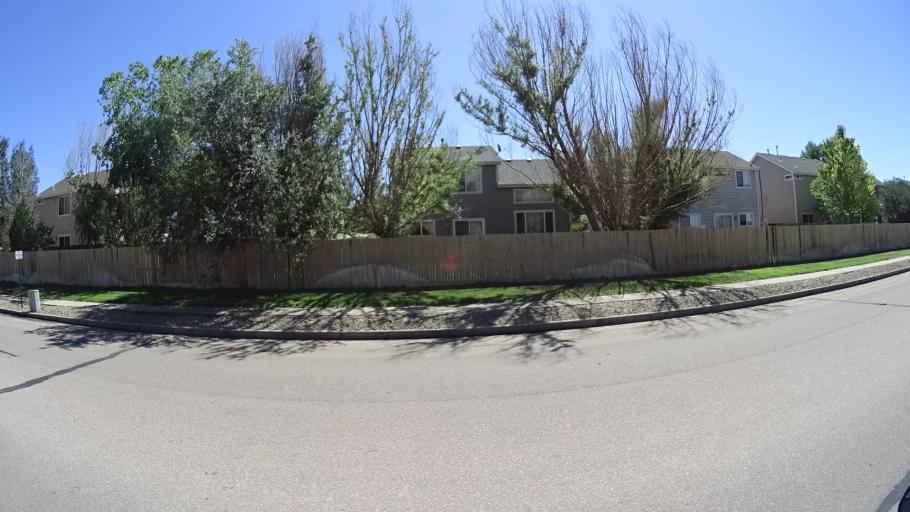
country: US
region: Colorado
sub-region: El Paso County
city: Security-Widefield
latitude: 38.7639
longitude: -104.6551
